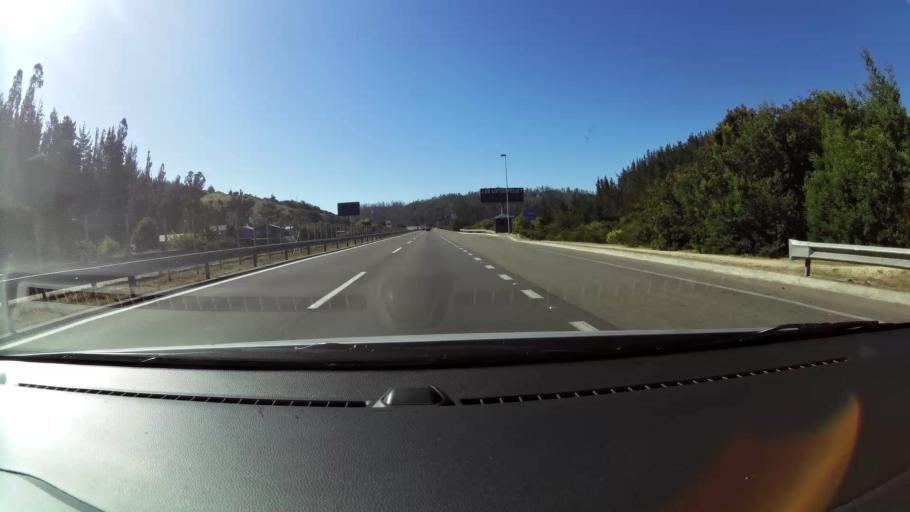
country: CL
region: Valparaiso
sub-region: Provincia de Marga Marga
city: Quilpue
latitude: -33.2201
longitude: -71.4713
